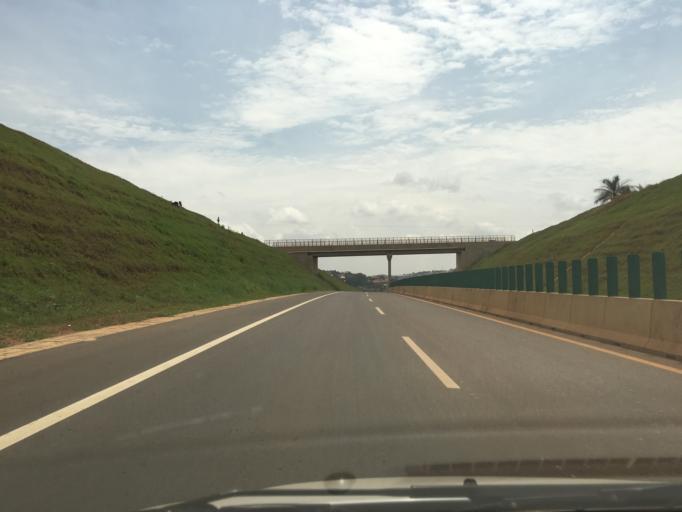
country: UG
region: Central Region
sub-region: Wakiso District
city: Kajansi
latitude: 0.1749
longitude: 32.5165
